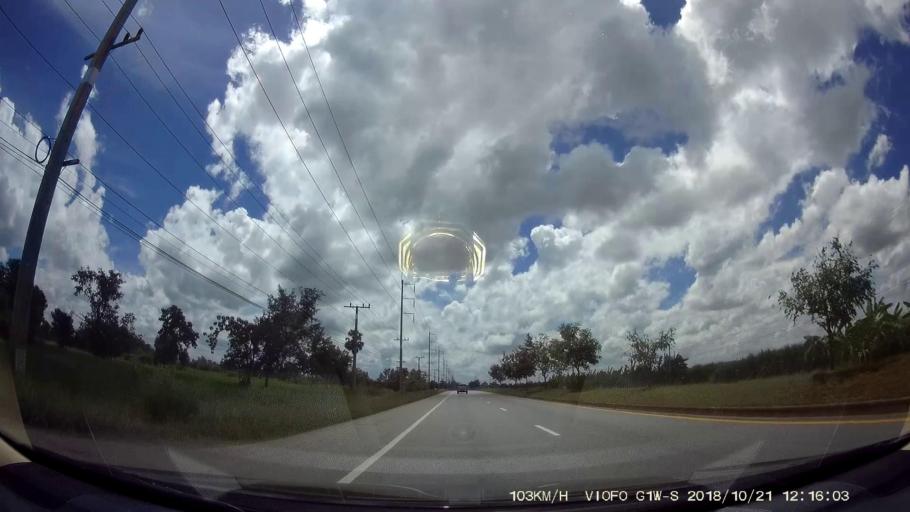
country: TH
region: Nakhon Ratchasima
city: Dan Khun Thot
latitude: 15.3532
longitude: 101.8275
